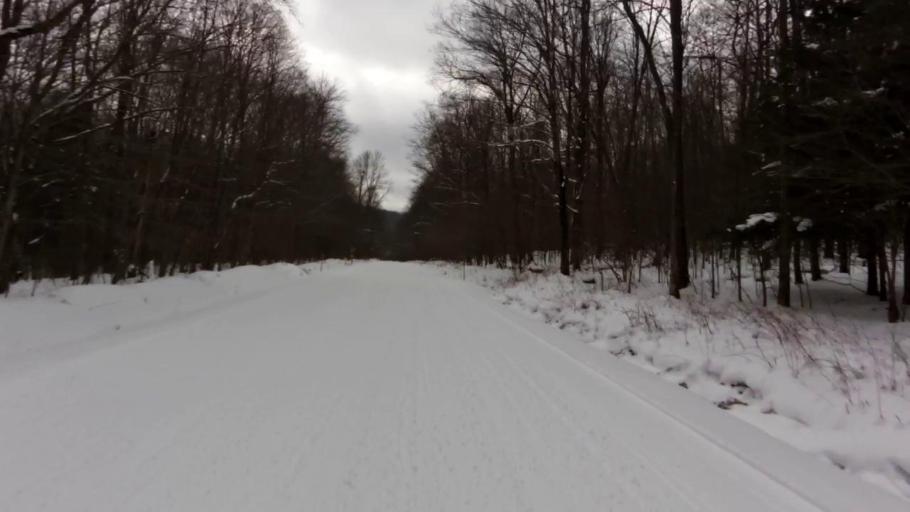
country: US
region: New York
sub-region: Cattaraugus County
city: Salamanca
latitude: 42.0267
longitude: -78.8141
